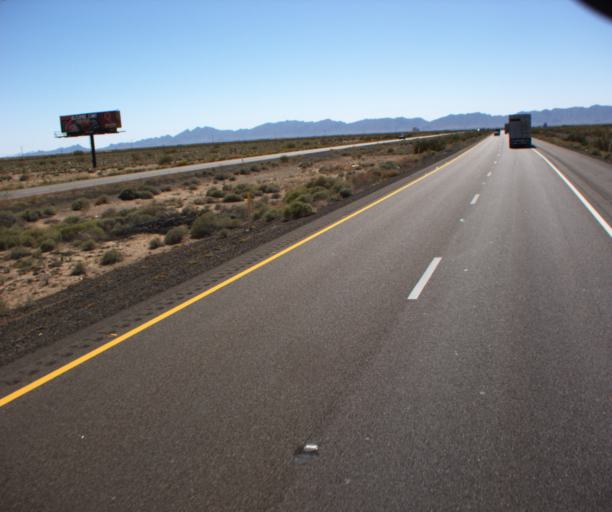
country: US
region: Arizona
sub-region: Yuma County
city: Wellton
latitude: 32.7971
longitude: -113.5488
